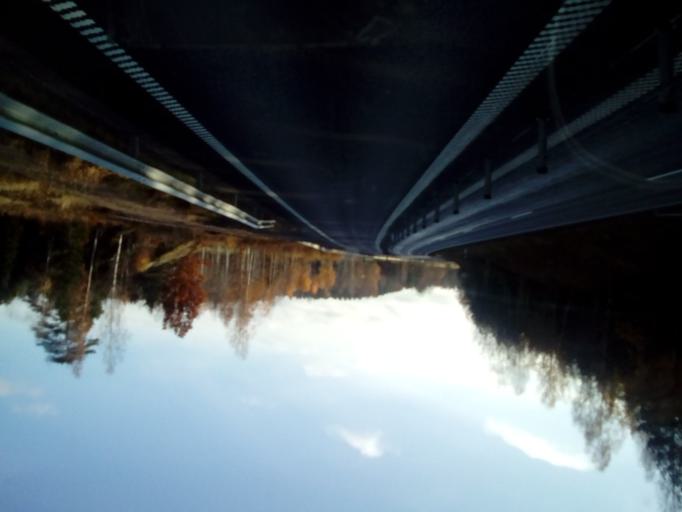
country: SE
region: Kalmar
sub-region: Vimmerby Kommun
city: Vimmerby
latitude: 57.7038
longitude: 16.0202
